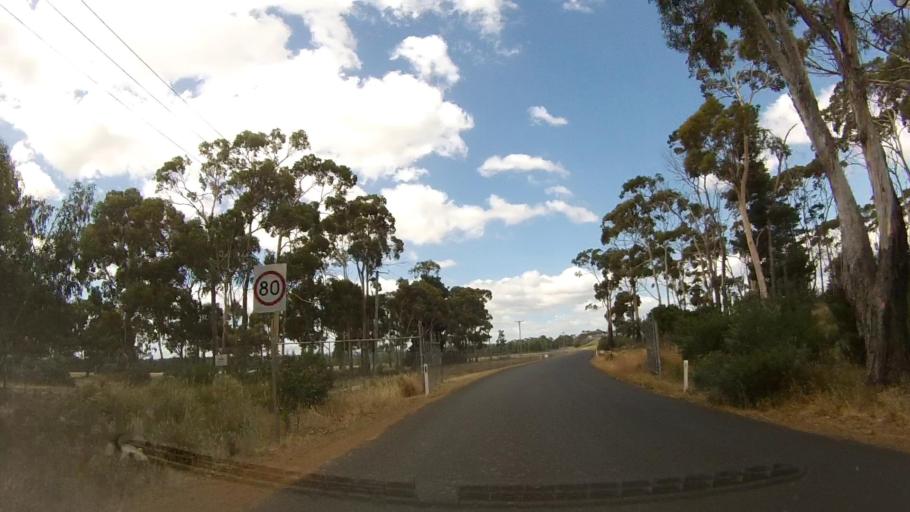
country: AU
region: Tasmania
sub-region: Clarence
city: Seven Mile Beach
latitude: -42.8486
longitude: 147.5221
